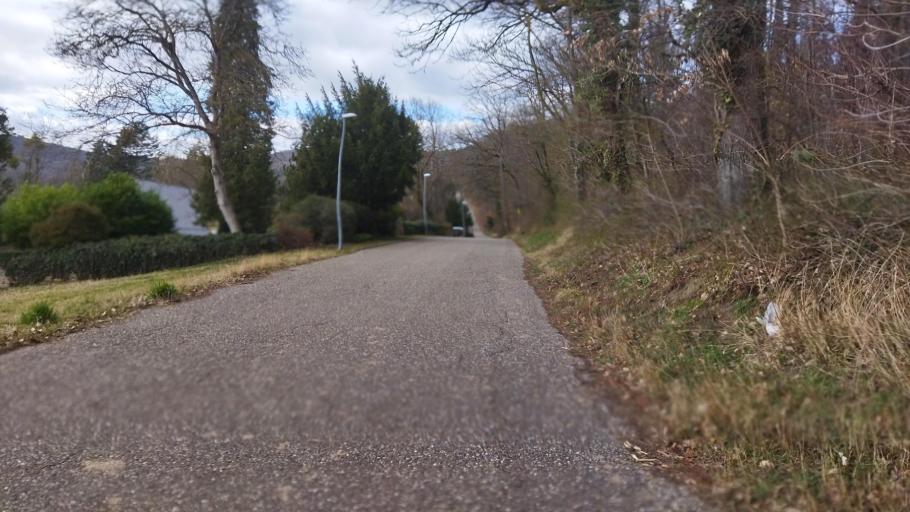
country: DE
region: Baden-Wuerttemberg
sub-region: Regierungsbezirk Stuttgart
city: Freudental
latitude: 49.0132
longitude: 9.0630
